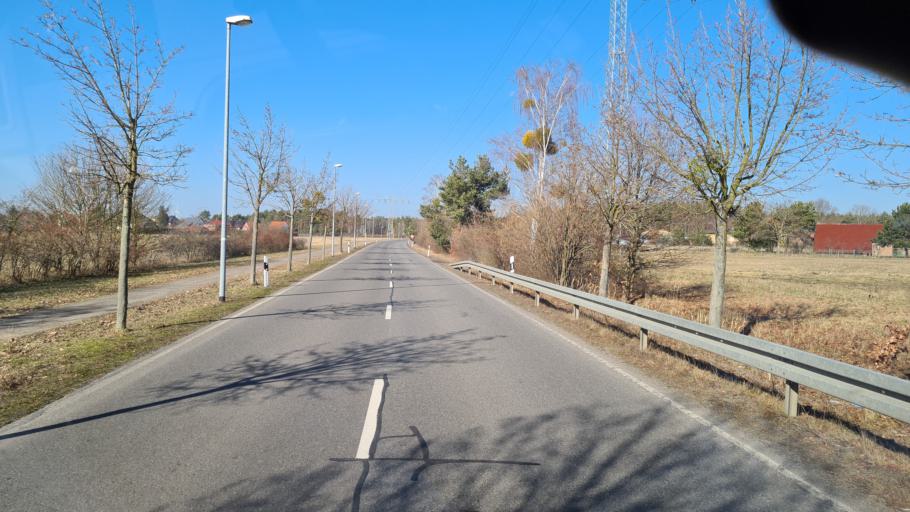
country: DE
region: Brandenburg
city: Grossraschen
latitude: 51.5852
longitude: 14.0319
